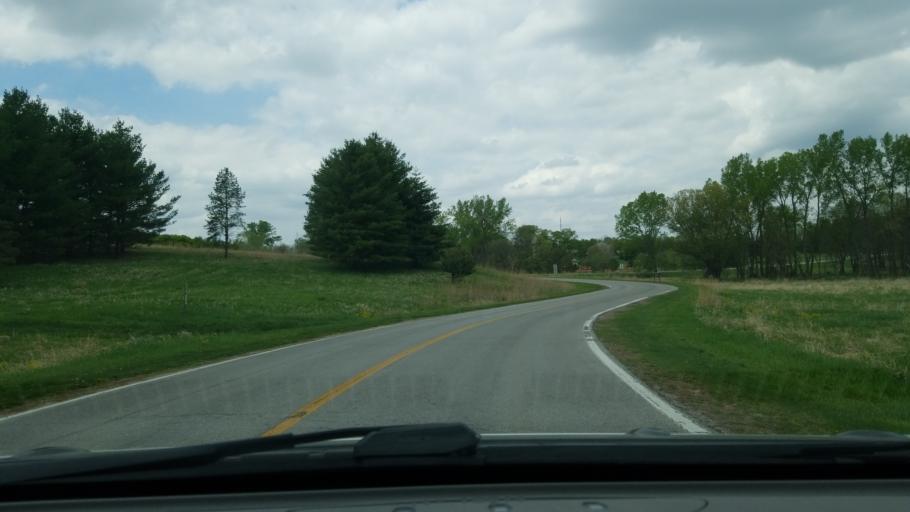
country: US
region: Nebraska
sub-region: Sarpy County
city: Chalco
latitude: 41.1687
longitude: -96.1600
